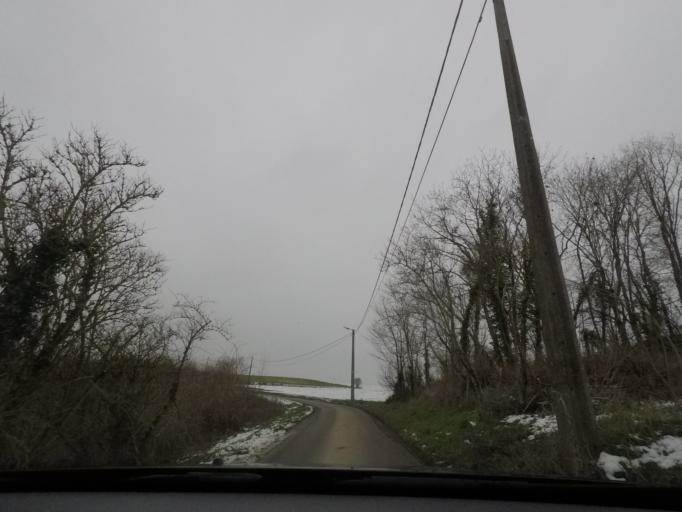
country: BE
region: Wallonia
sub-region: Province du Hainaut
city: Brugelette
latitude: 50.5927
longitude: 3.8838
